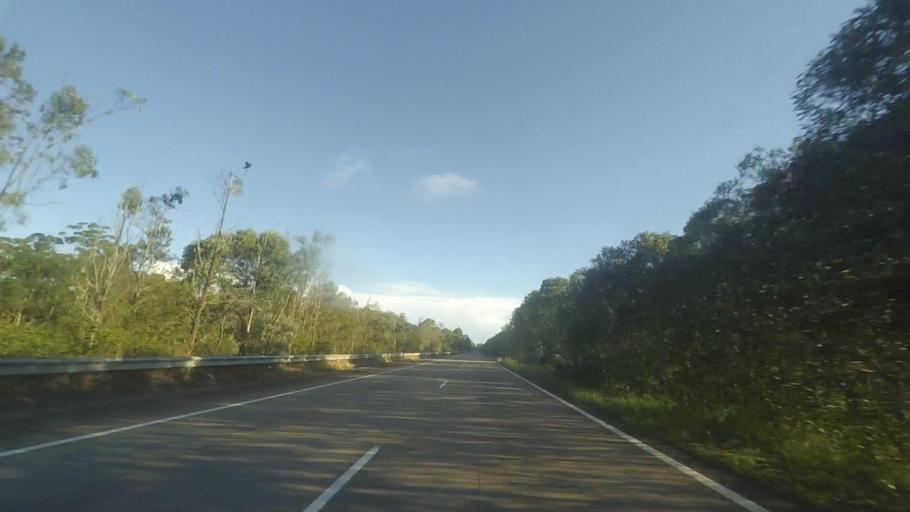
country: AU
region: New South Wales
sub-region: Great Lakes
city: Bulahdelah
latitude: -32.2908
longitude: 152.3425
